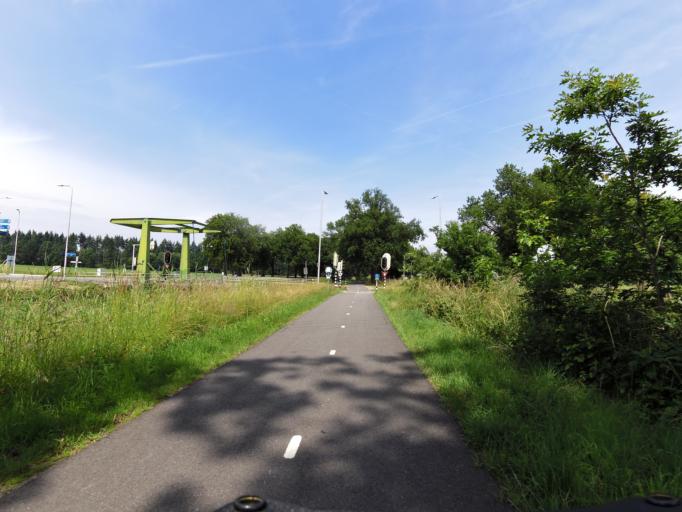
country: NL
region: Gelderland
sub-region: Gemeente Apeldoorn
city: Loenen
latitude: 52.1396
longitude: 6.0412
